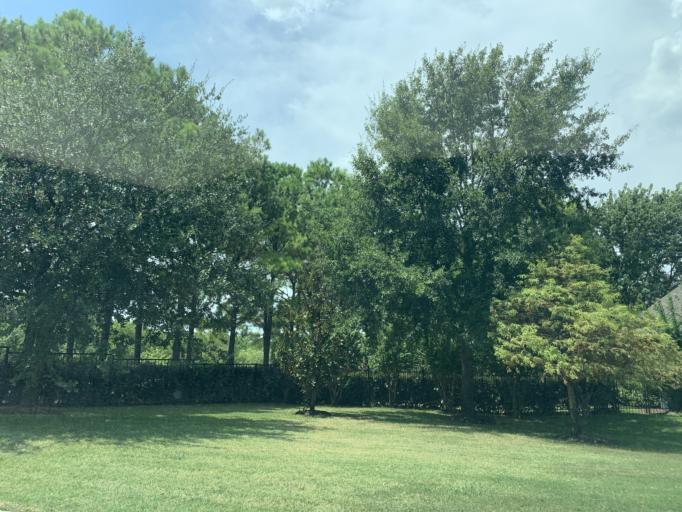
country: US
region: Texas
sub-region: Denton County
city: Trophy Club
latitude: 32.9744
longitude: -97.1551
